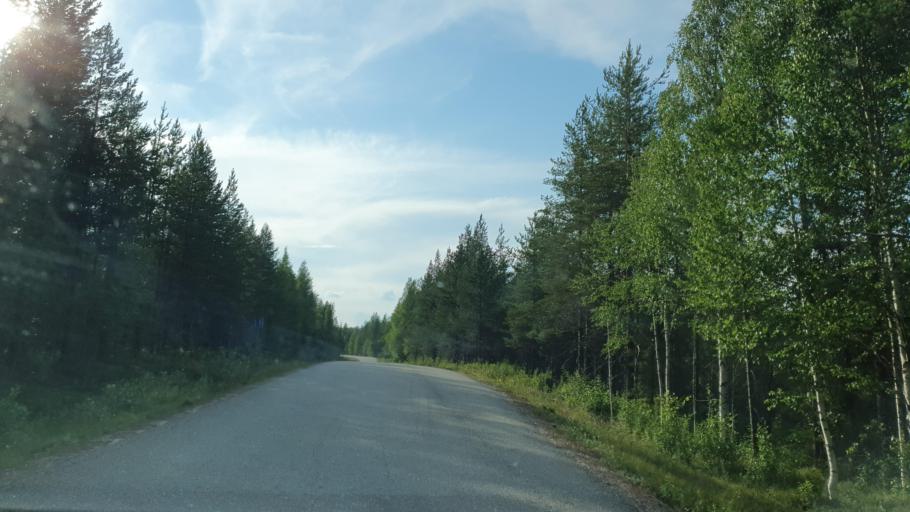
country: FI
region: Kainuu
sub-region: Kehys-Kainuu
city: Kuhmo
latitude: 64.2782
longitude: 29.4291
